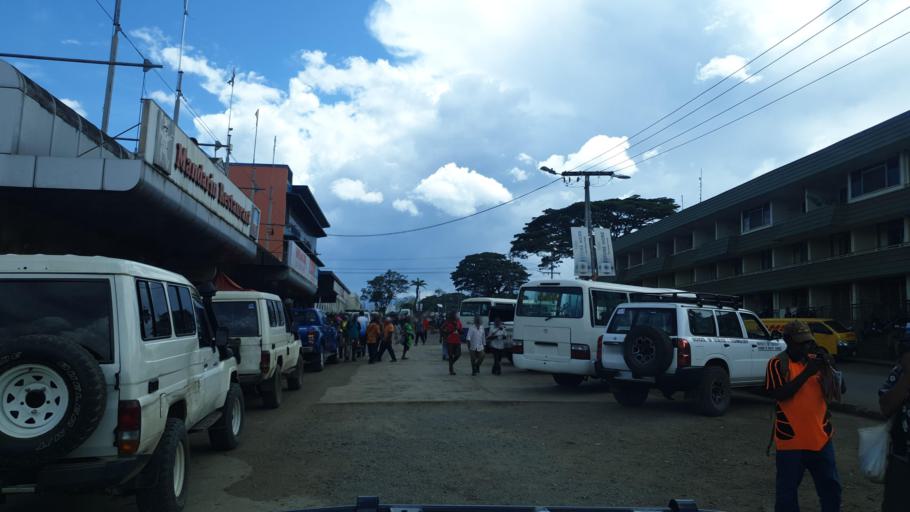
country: PG
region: Eastern Highlands
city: Goroka
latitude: -6.0730
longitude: 145.3952
